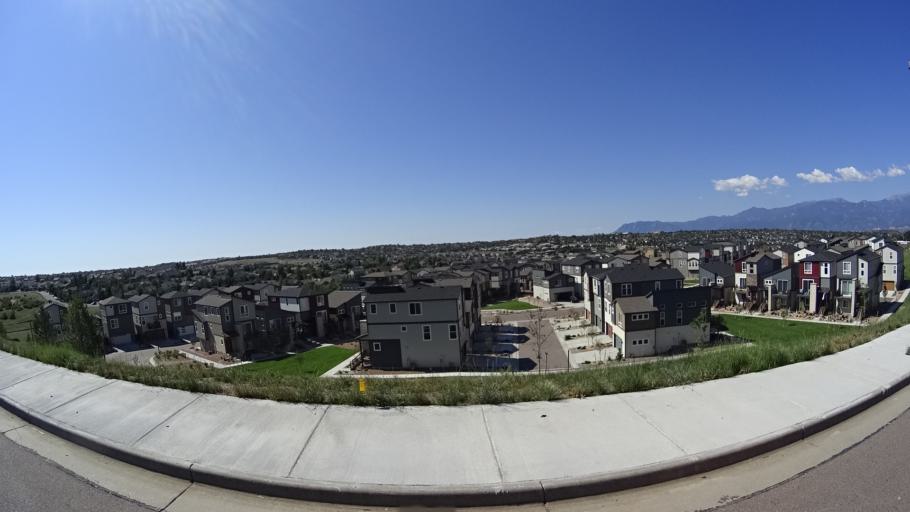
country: US
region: Colorado
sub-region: El Paso County
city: Black Forest
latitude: 38.9381
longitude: -104.7493
